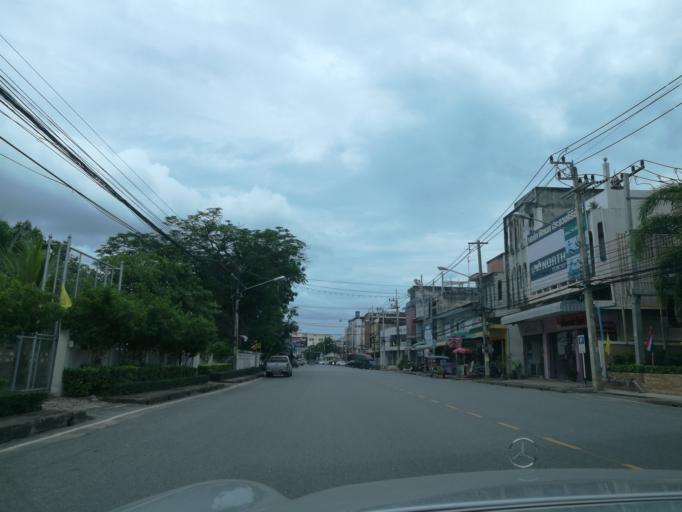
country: TH
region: Prachuap Khiri Khan
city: Prachuap Khiri Khan
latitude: 11.8062
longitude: 99.7973
